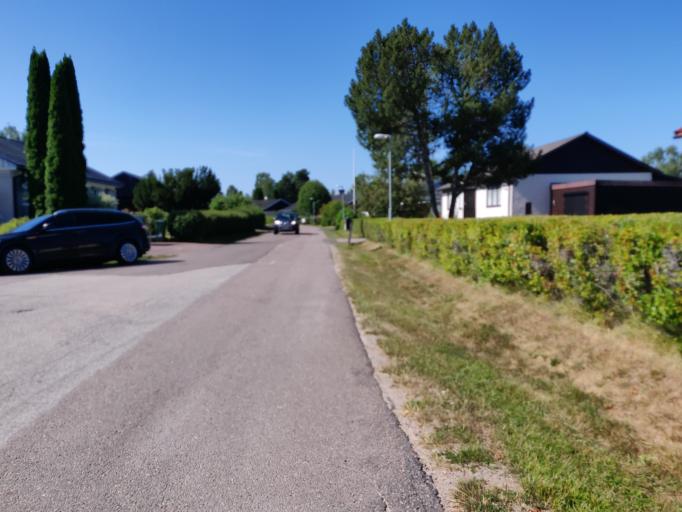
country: SE
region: Vaermland
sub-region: Hagfors Kommun
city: Hagfors
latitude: 60.0005
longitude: 13.5896
